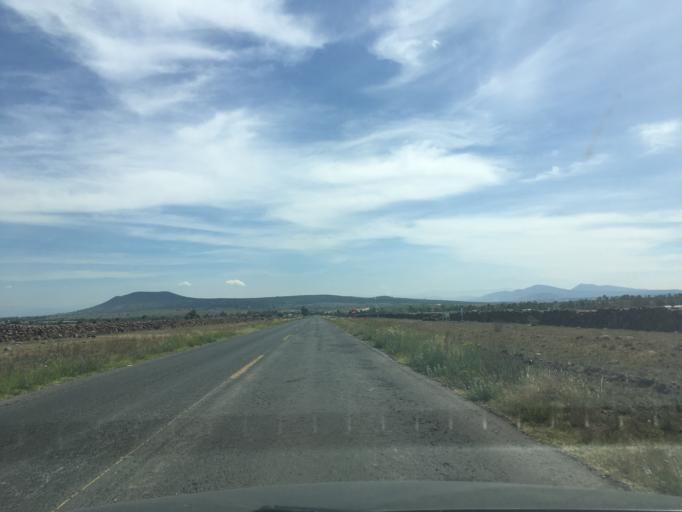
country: MX
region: Queretaro
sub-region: San Juan del Rio
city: El Jazmin
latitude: 20.2537
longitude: -100.0739
